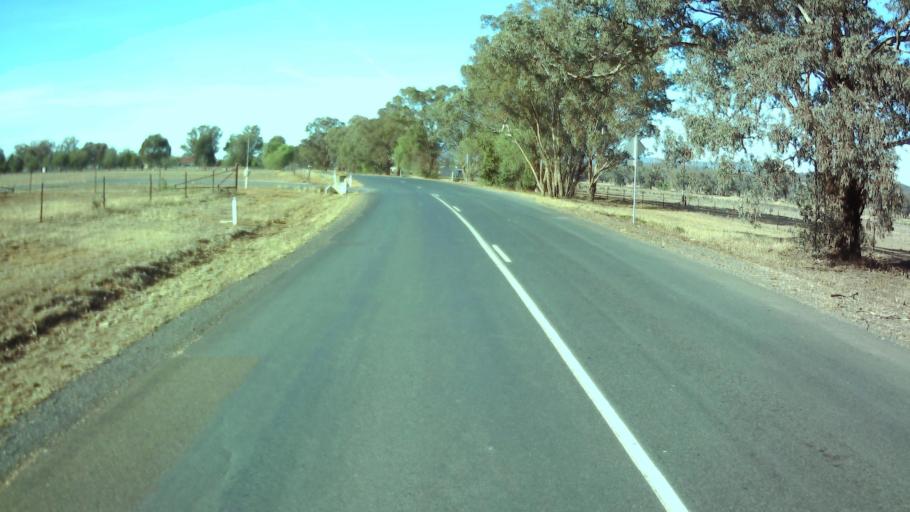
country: AU
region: New South Wales
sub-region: Weddin
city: Grenfell
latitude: -33.9071
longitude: 148.1466
